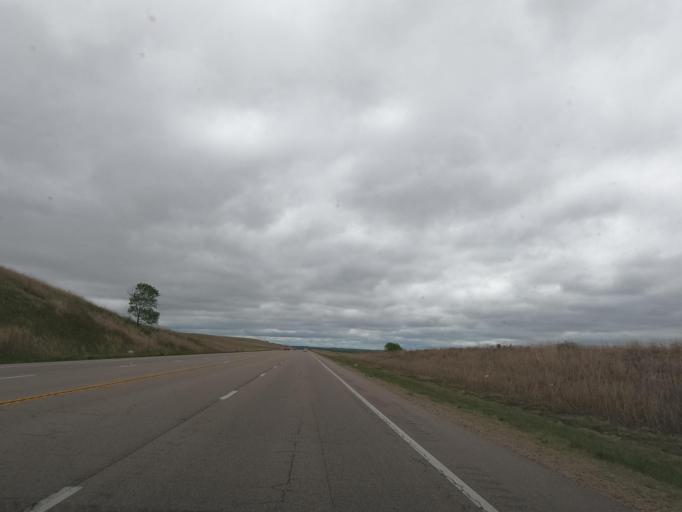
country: US
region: Kansas
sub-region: Greenwood County
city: Eureka
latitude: 37.6422
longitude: -96.4152
